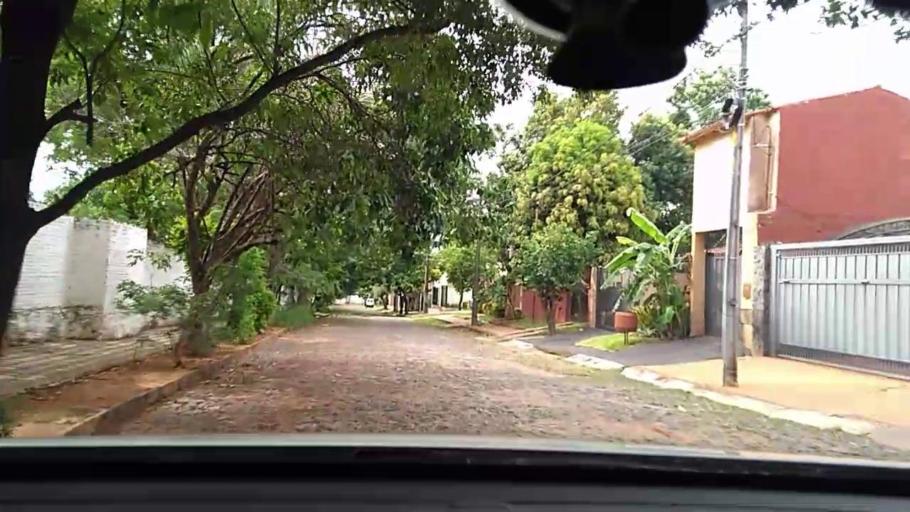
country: PY
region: Asuncion
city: Asuncion
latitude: -25.2702
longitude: -57.5791
